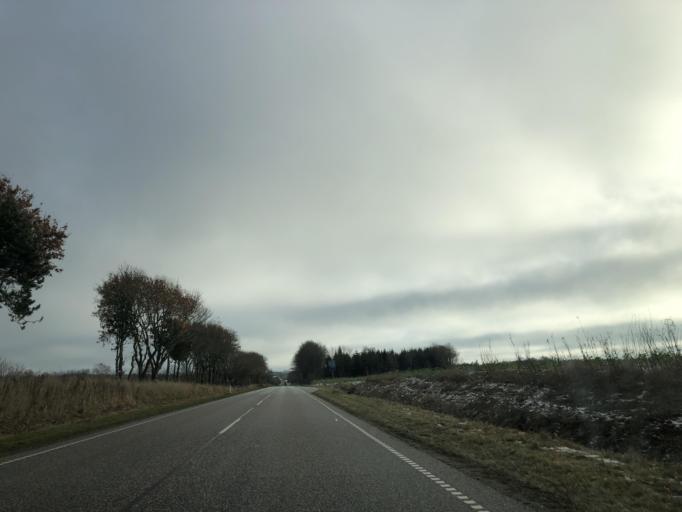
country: DK
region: Central Jutland
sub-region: Horsens Kommune
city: Braedstrup
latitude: 55.9068
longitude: 9.5932
